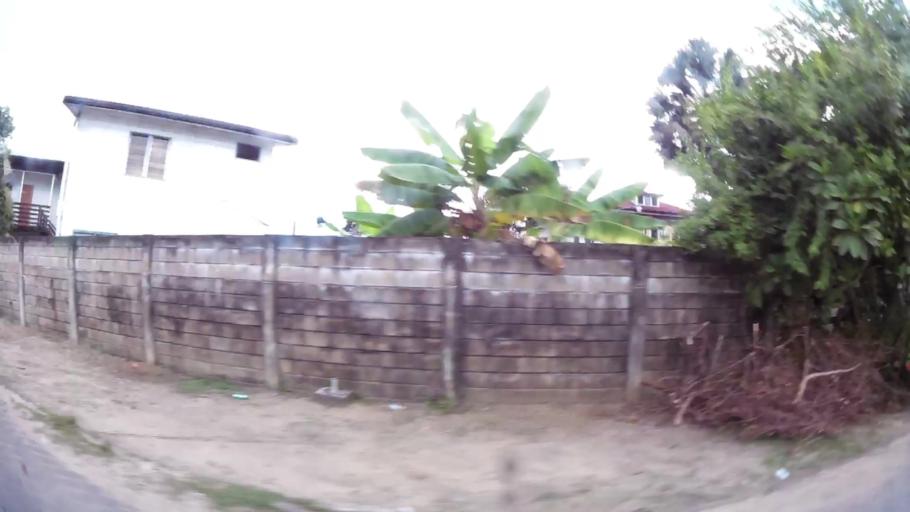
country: SR
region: Paramaribo
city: Paramaribo
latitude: 5.8293
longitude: -55.1487
